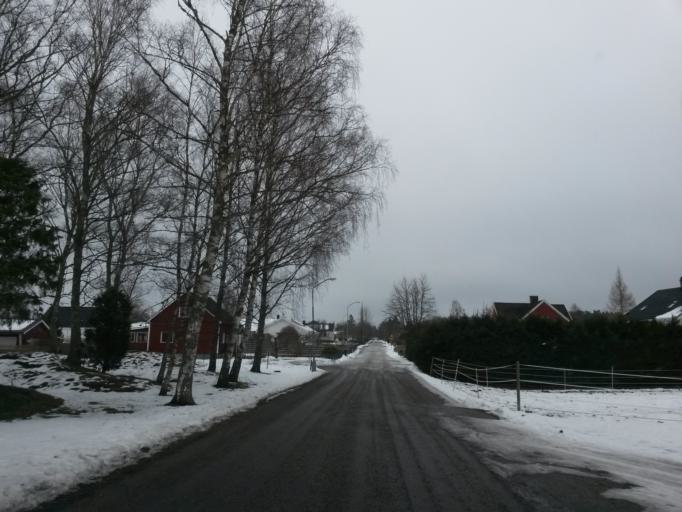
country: SE
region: Vaestra Goetaland
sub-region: Herrljunga Kommun
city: Herrljunga
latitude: 57.9842
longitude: 13.0565
